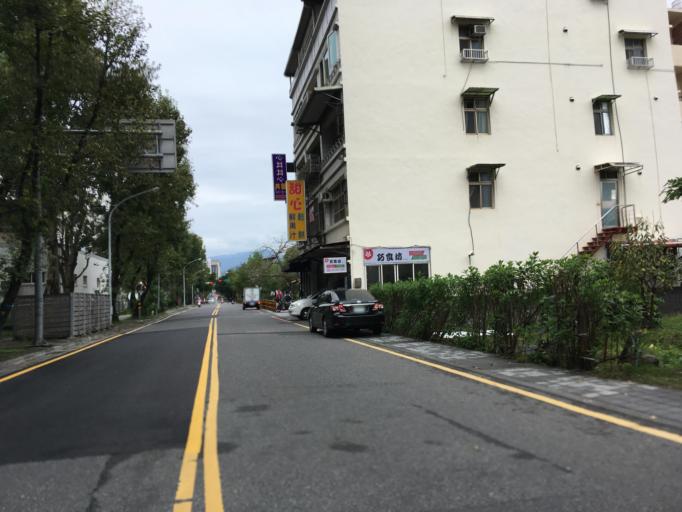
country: TW
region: Taiwan
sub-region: Yilan
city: Yilan
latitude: 24.7471
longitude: 121.7488
